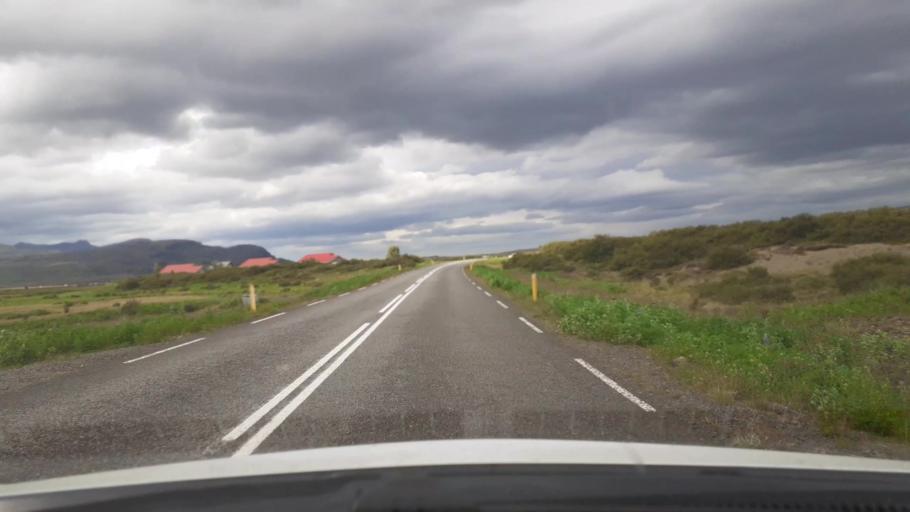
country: IS
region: West
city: Borgarnes
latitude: 64.5432
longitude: -21.6245
